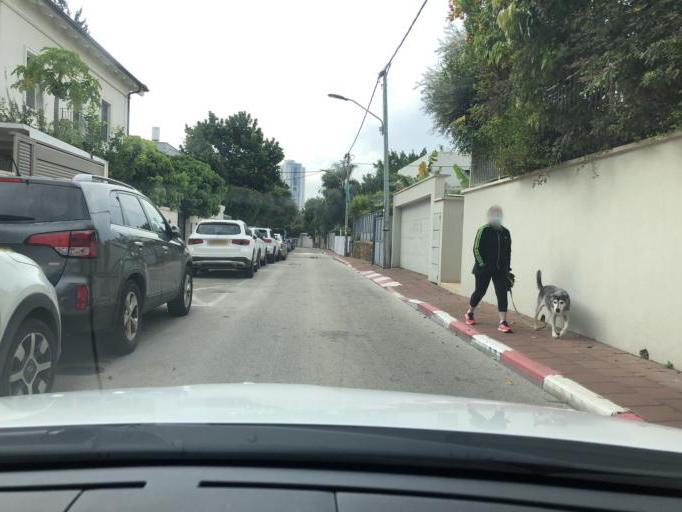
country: IL
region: Tel Aviv
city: Giv`atayim
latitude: 32.0548
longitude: 34.8200
